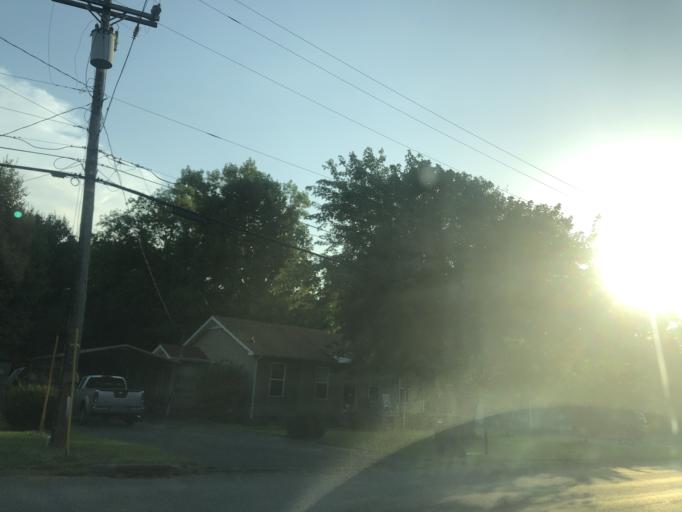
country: US
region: Tennessee
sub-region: Davidson County
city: Lakewood
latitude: 36.1404
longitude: -86.6389
